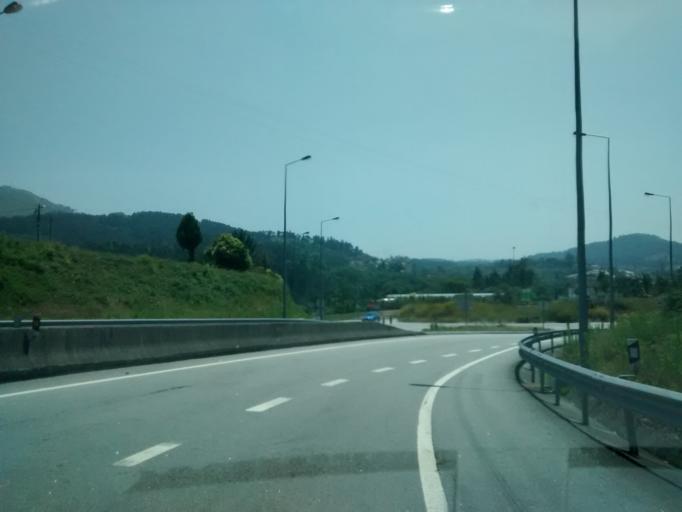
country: PT
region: Viana do Castelo
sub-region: Ponte de Lima
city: Ponte de Lima
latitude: 41.7811
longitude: -8.5553
